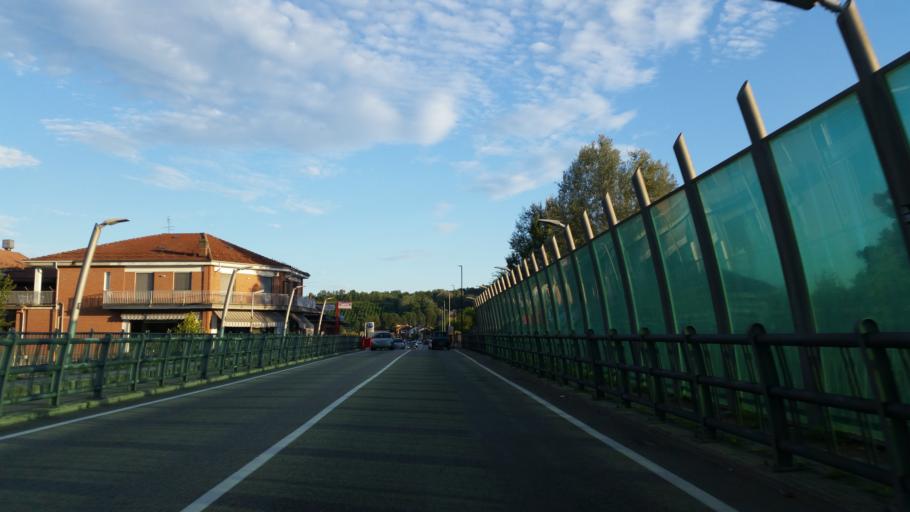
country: IT
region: Piedmont
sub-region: Provincia di Asti
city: Asti
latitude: 44.8847
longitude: 8.2123
